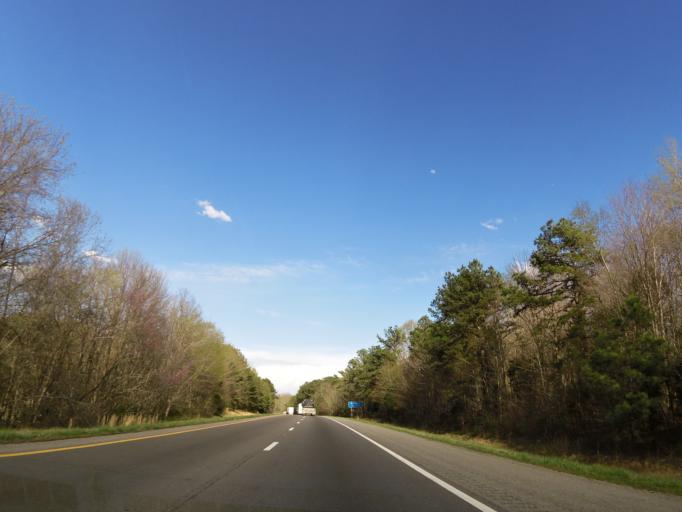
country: US
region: Tennessee
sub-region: Dickson County
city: Dickson
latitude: 36.0087
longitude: -87.3890
